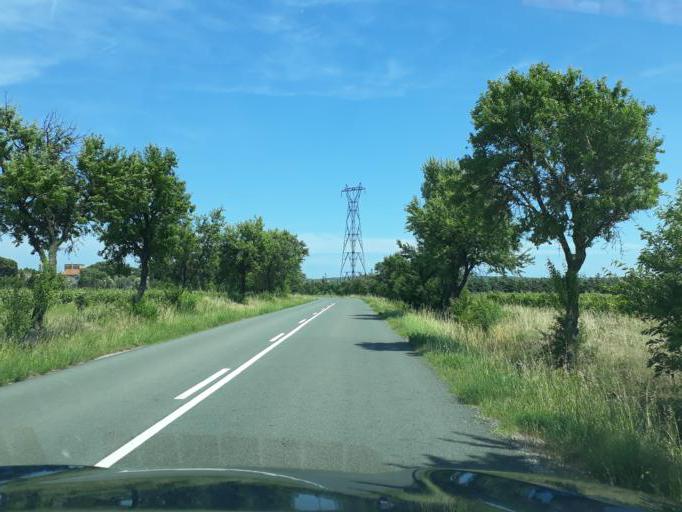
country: FR
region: Languedoc-Roussillon
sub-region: Departement de l'Aude
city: Portel-des-Corbieres
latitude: 43.0404
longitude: 2.9399
